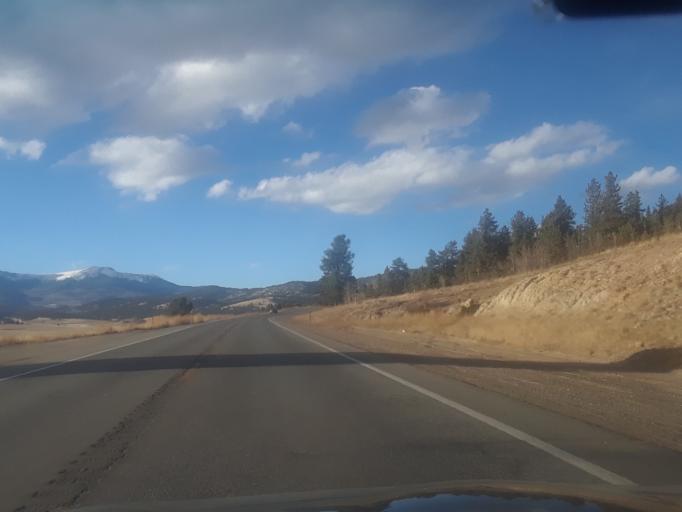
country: US
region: Colorado
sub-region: Chaffee County
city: Buena Vista
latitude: 38.8846
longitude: -105.9903
